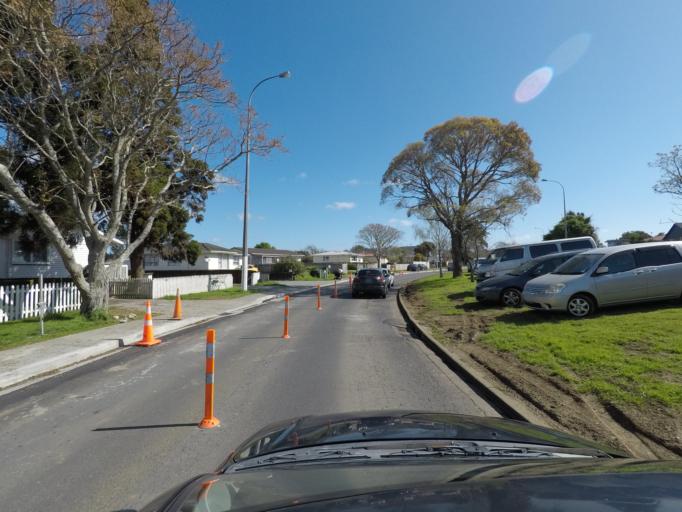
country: NZ
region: Auckland
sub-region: Auckland
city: Rosebank
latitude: -36.8571
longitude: 174.6195
